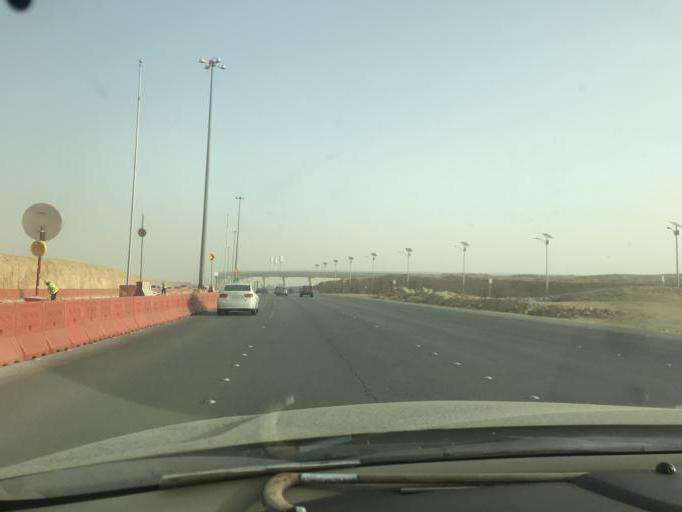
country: SA
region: Ar Riyad
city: Riyadh
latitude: 24.8707
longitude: 46.6950
